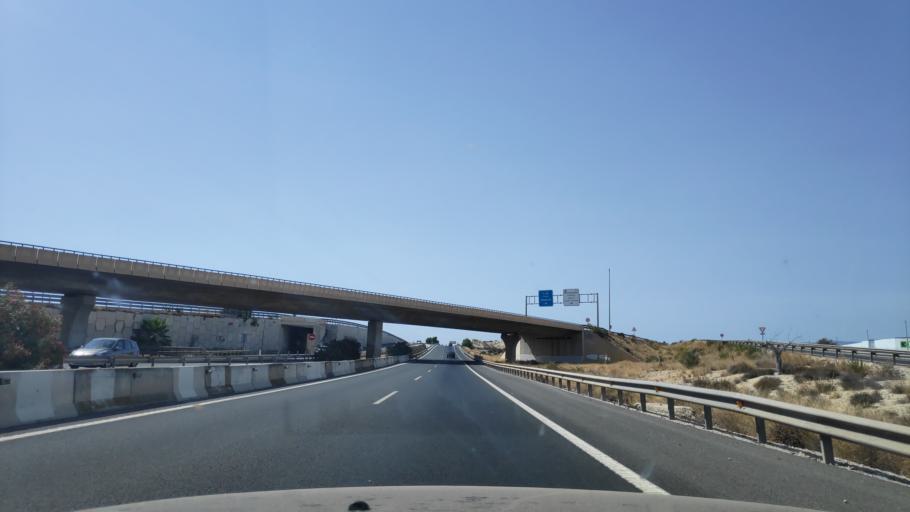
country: ES
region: Murcia
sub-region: Murcia
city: Lorqui
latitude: 38.0993
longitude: -1.2310
